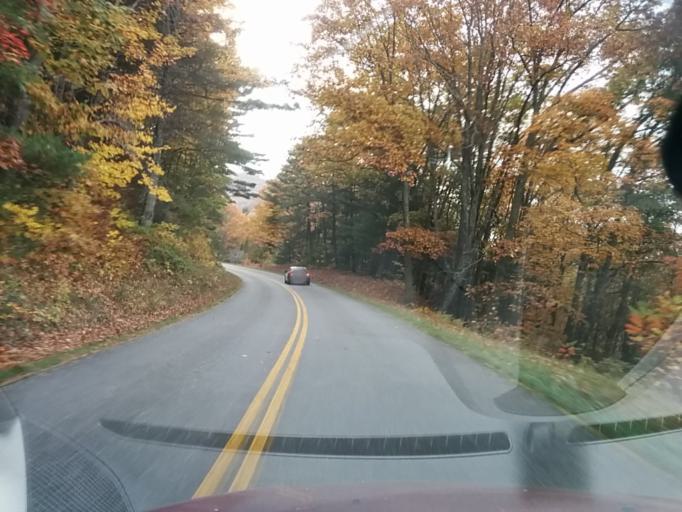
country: US
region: Virginia
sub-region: City of Buena Vista
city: Buena Vista
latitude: 37.8066
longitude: -79.2459
